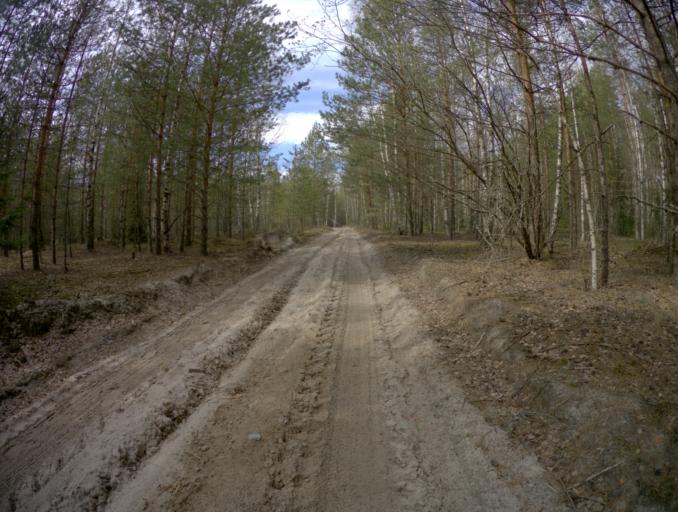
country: RU
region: Vladimir
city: Urshel'skiy
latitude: 55.8665
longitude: 40.1953
